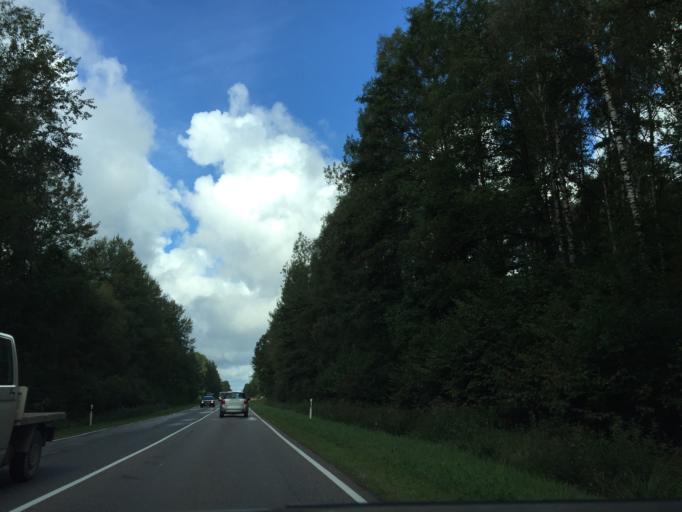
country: LV
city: Tireli
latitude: 56.9272
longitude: 23.5319
